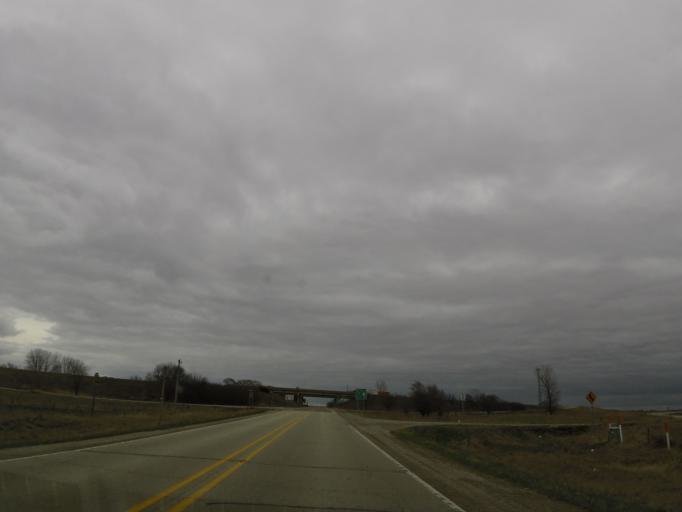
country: US
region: Iowa
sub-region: Benton County
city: Urbana
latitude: 42.3120
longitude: -91.9809
